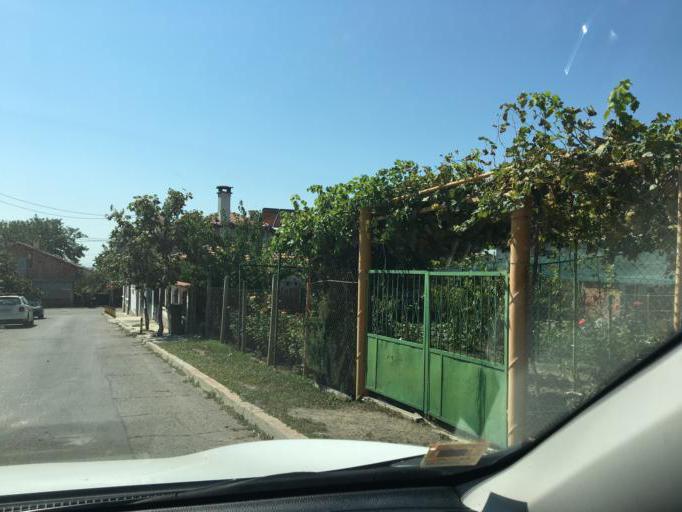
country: BG
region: Burgas
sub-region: Obshtina Kameno
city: Kameno
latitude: 42.6284
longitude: 27.3937
